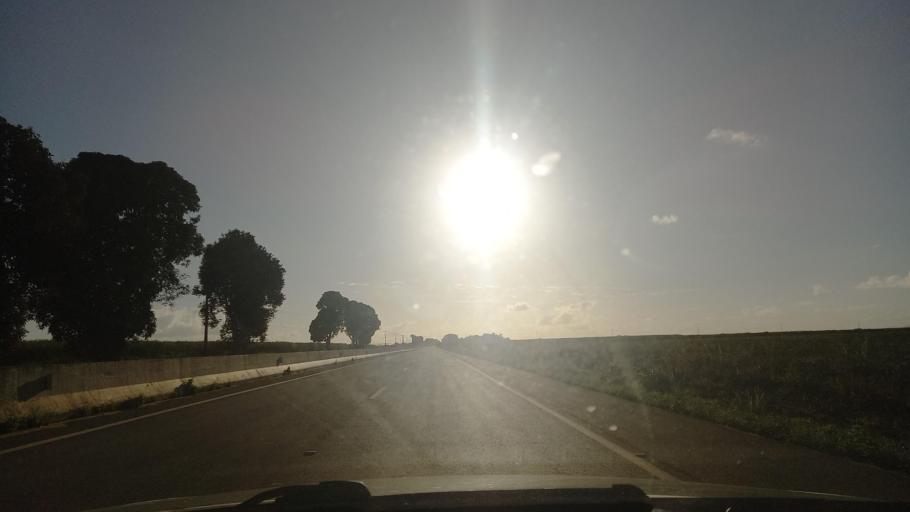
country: BR
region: Alagoas
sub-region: Campo Alegre
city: Campo Alegre
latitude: -9.7940
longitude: -36.3109
